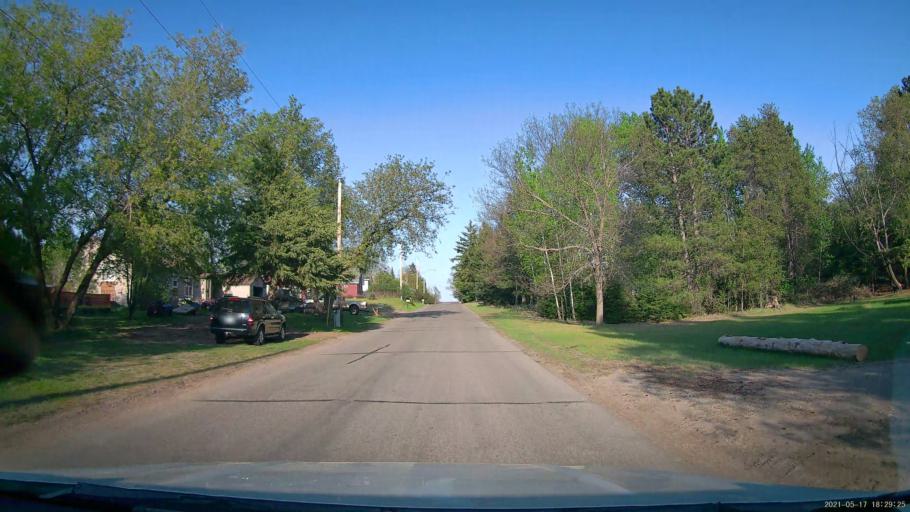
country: US
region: Minnesota
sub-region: Hubbard County
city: Park Rapids
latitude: 46.9253
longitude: -95.0473
